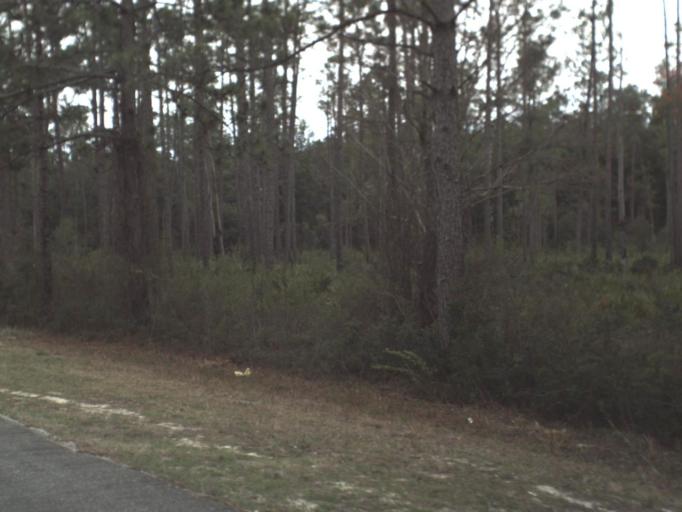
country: US
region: Florida
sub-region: Gadsden County
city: Midway
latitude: 30.3704
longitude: -84.5484
